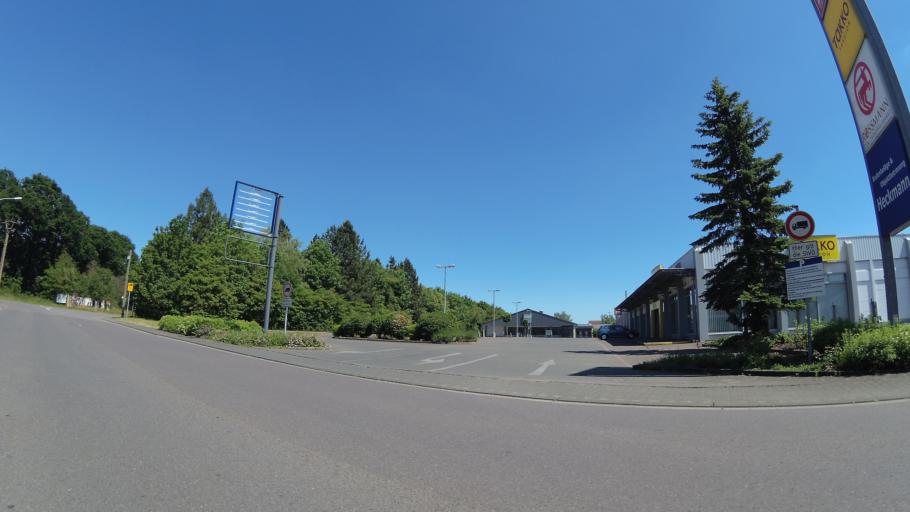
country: DE
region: Saarland
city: Saarwellingen
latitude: 49.3585
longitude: 6.7926
